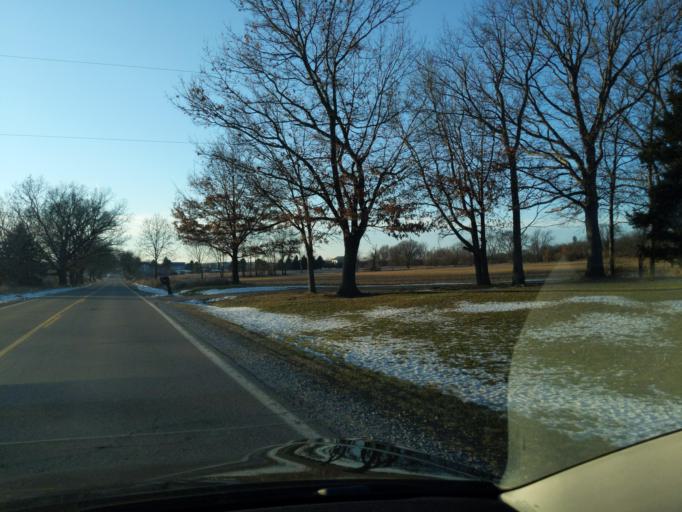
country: US
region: Michigan
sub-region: Ingham County
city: Stockbridge
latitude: 42.4679
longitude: -84.1238
